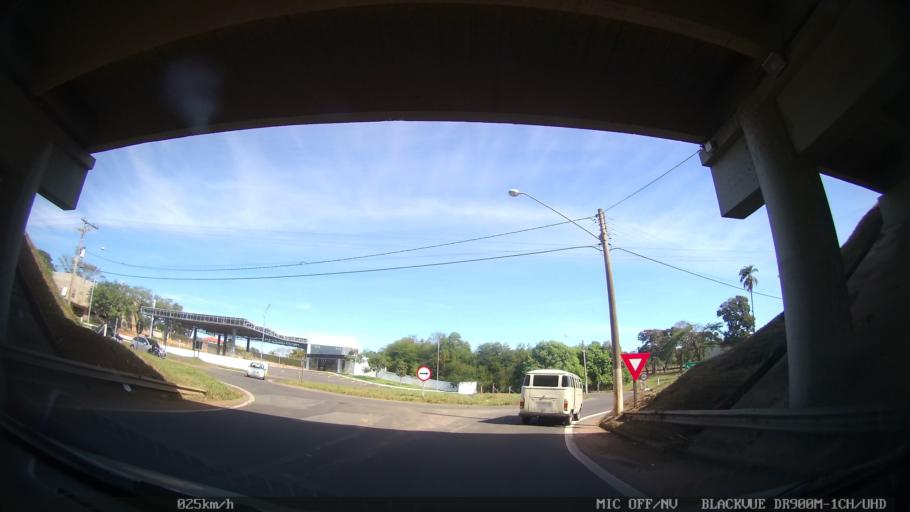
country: BR
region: Sao Paulo
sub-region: Porto Ferreira
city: Porto Ferreira
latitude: -21.8661
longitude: -47.4909
